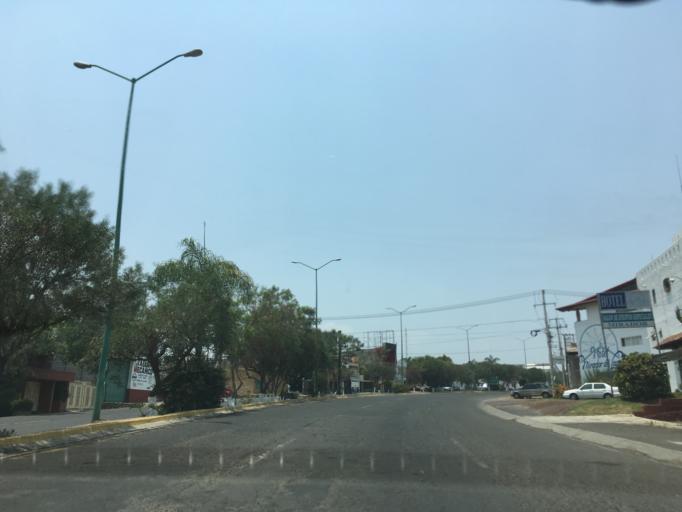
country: MX
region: Michoacan
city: Patzcuaro
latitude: 19.5246
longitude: -101.6152
